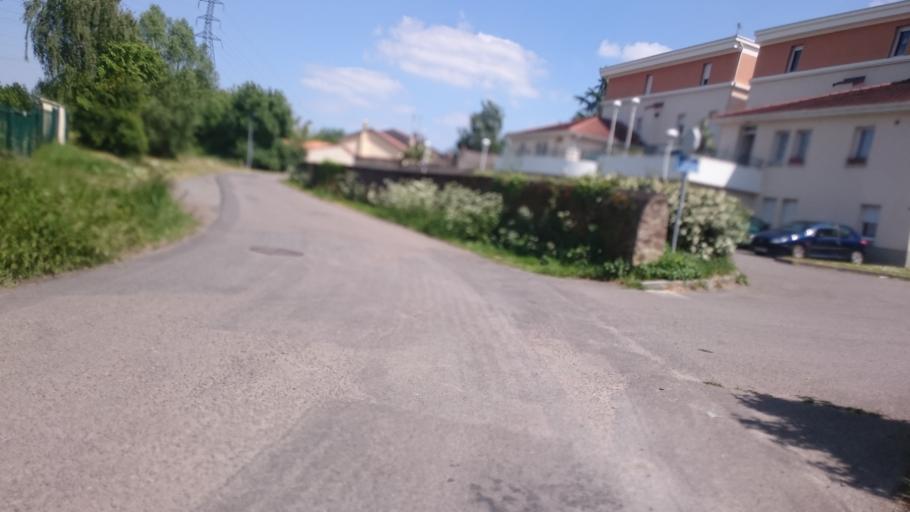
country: FR
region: Pays de la Loire
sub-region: Departement de la Loire-Atlantique
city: Bouguenais
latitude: 47.1813
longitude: -1.6256
